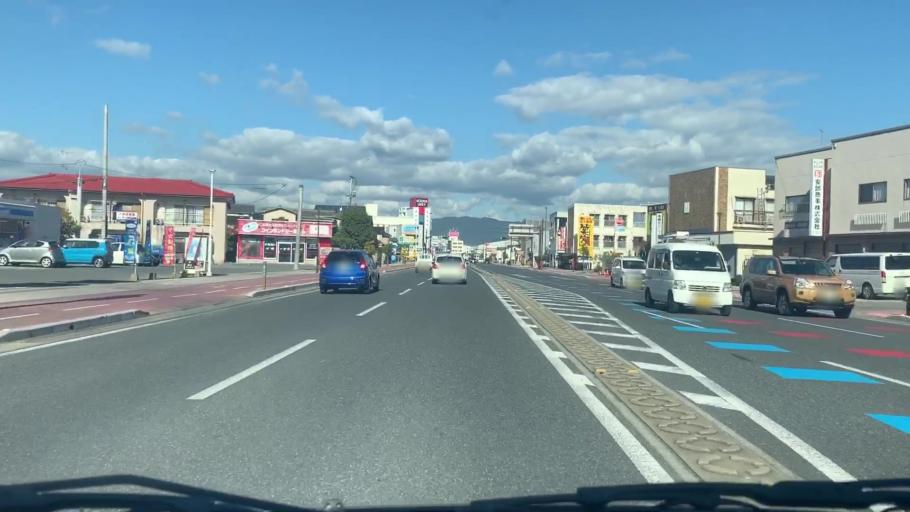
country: JP
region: Saga Prefecture
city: Saga-shi
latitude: 33.2672
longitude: 130.2937
